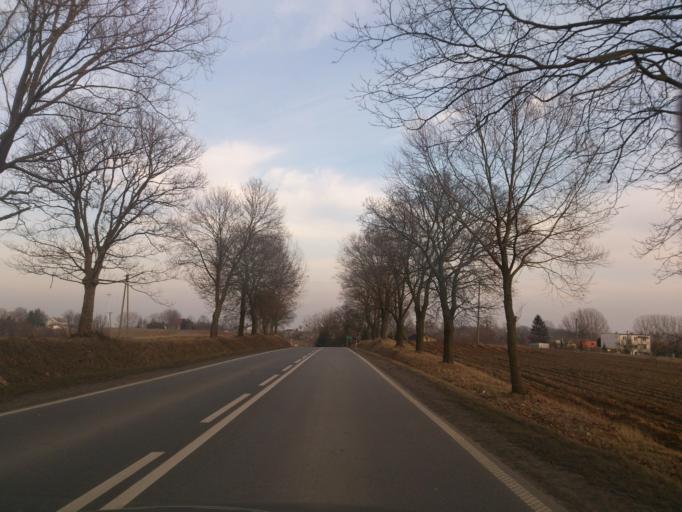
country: PL
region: Kujawsko-Pomorskie
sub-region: Powiat rypinski
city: Ostrowite
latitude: 53.0691
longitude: 19.3073
